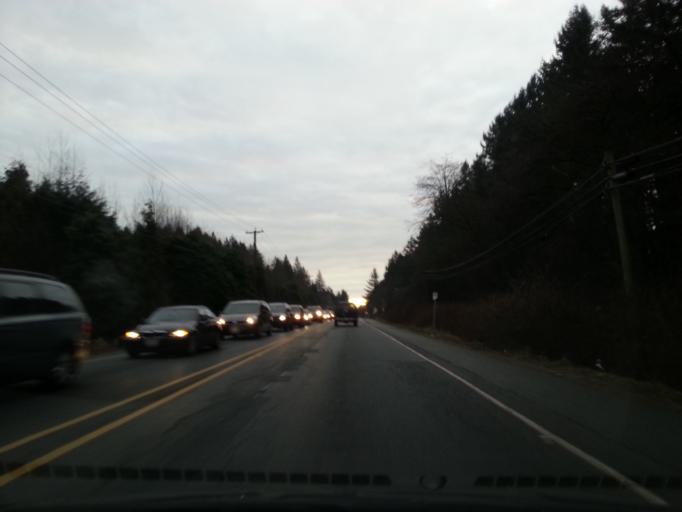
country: CA
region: British Columbia
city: Surrey
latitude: 49.1781
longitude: -122.8326
